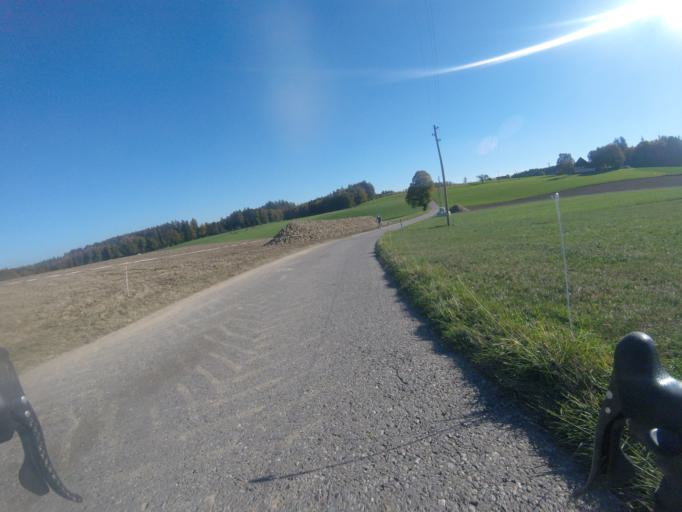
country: CH
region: Bern
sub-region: Seeland District
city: Schupfen
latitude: 47.0209
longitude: 7.3954
